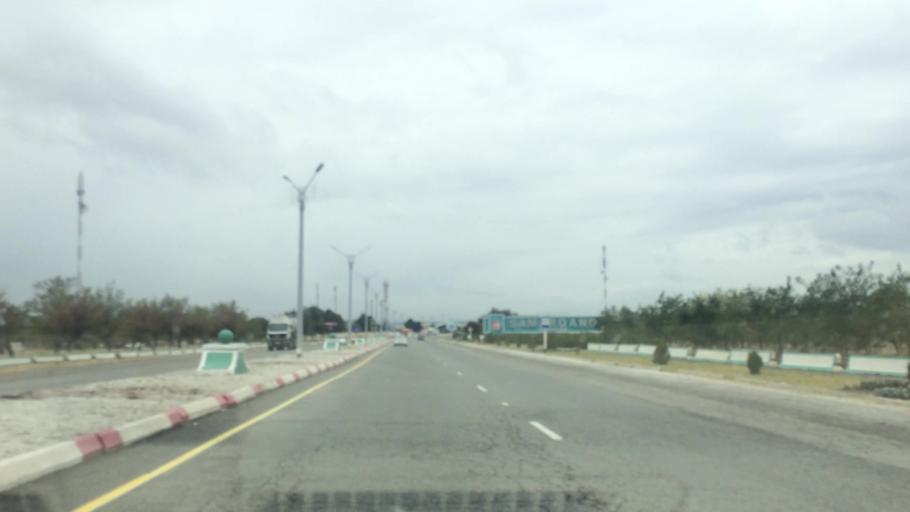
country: UZ
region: Samarqand
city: Bulung'ur
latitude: 39.8530
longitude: 67.4642
